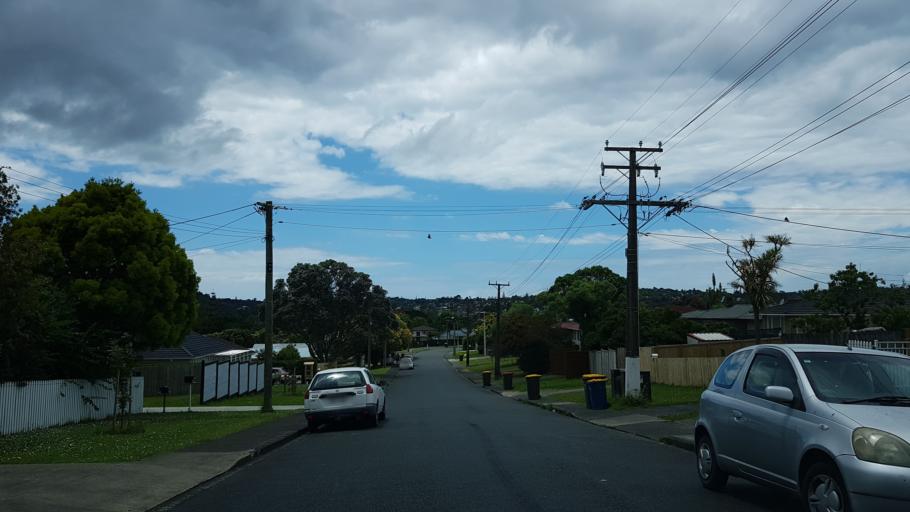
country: NZ
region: Auckland
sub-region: Auckland
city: North Shore
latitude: -36.7942
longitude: 174.6927
